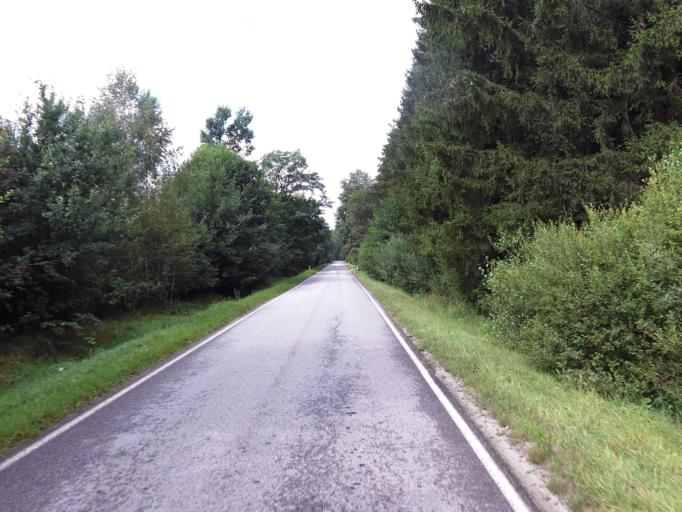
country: CZ
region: Jihocesky
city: Suchdol nad Luznici
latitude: 48.8651
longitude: 14.8513
